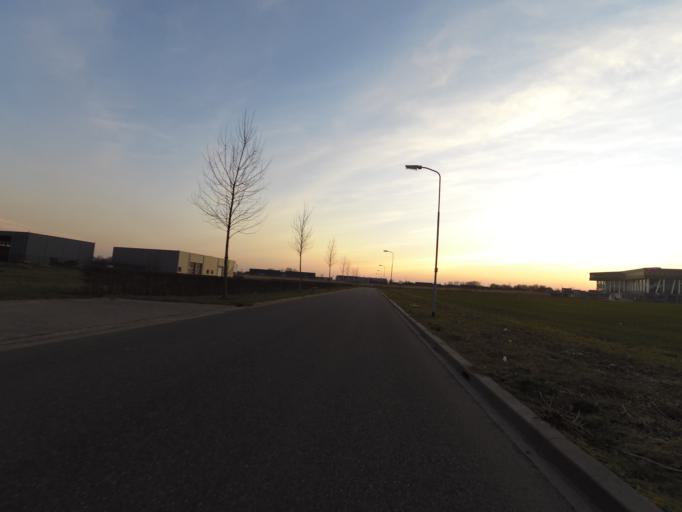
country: NL
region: Gelderland
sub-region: Gemeente Zevenaar
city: Zevenaar
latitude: 51.9234
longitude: 6.1063
